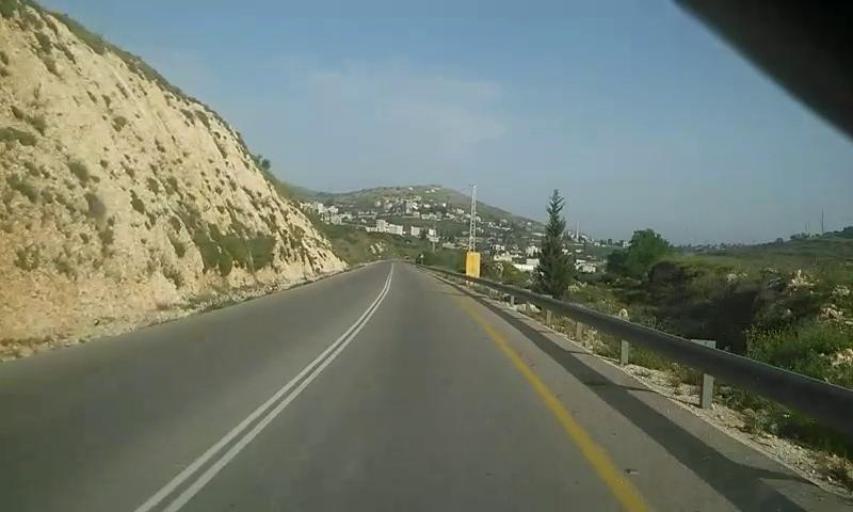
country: PS
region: West Bank
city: Madama
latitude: 32.1844
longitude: 35.2371
